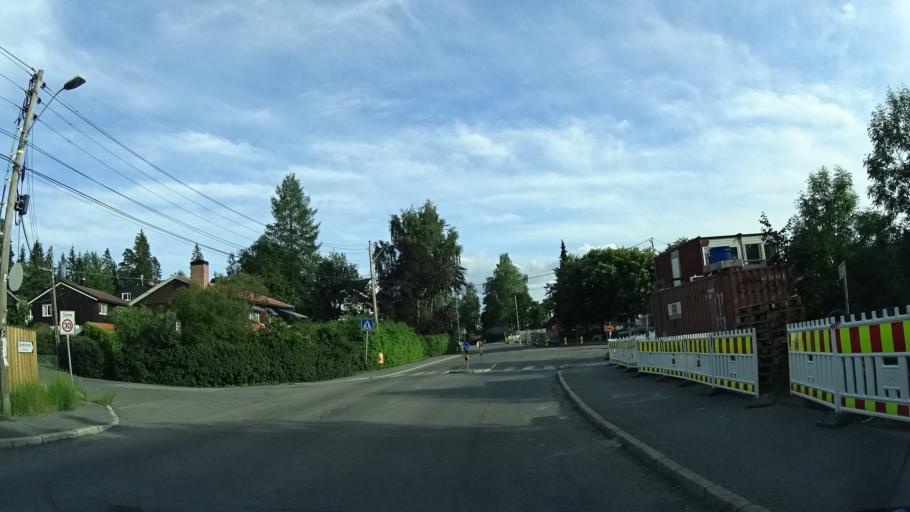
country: NO
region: Oslo
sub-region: Oslo
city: Sjolyststranda
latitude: 59.9545
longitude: 10.6577
